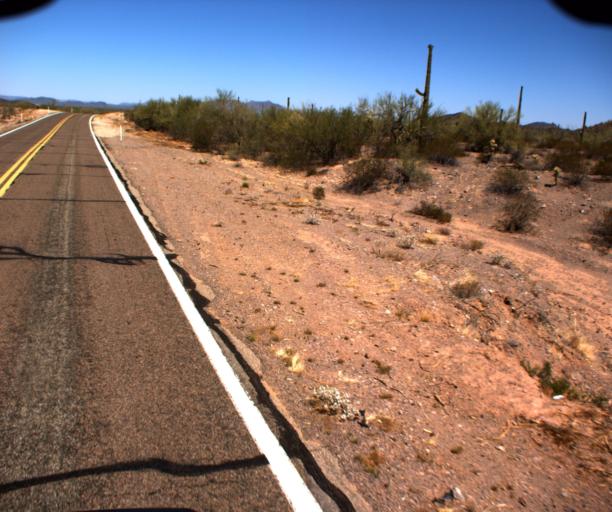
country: US
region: Arizona
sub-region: Pima County
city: Ajo
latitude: 32.2236
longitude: -112.7003
